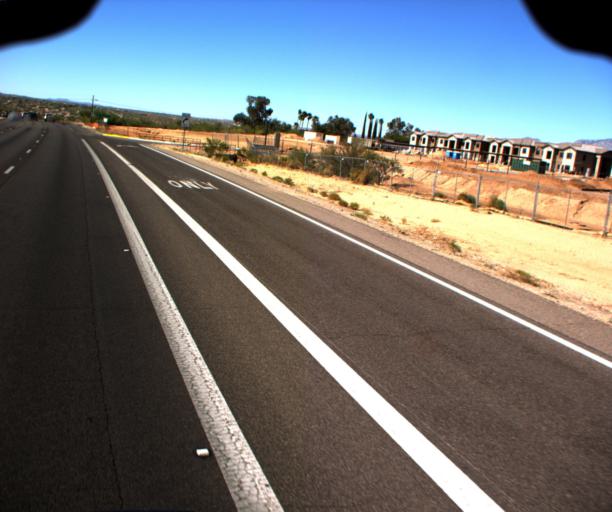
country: US
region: Arizona
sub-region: Pima County
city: Oro Valley
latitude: 32.3820
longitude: -110.9638
